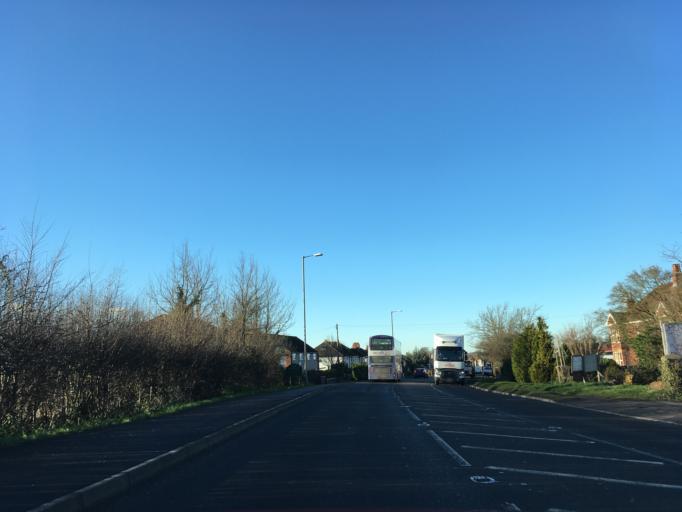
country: GB
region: England
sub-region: Bath and North East Somerset
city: Saltford
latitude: 51.4082
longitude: -2.4716
